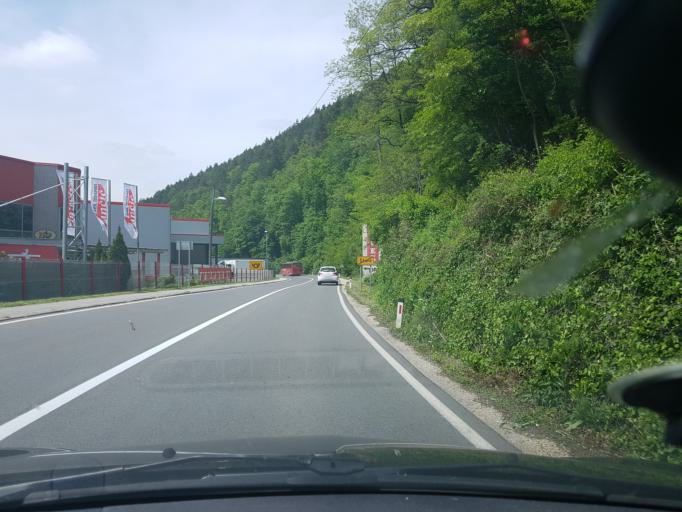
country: SI
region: Store
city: Store
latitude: 46.2231
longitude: 15.3170
